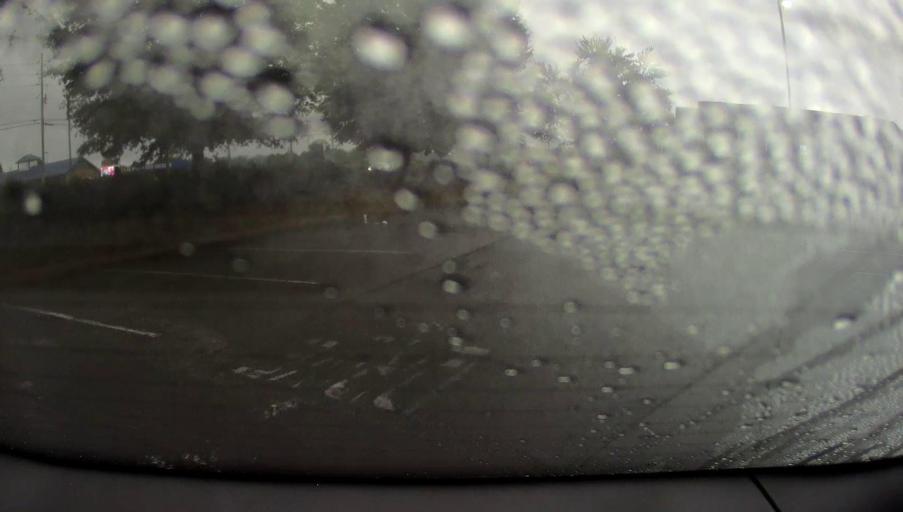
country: US
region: Georgia
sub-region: Houston County
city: Centerville
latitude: 32.5537
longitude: -83.6626
